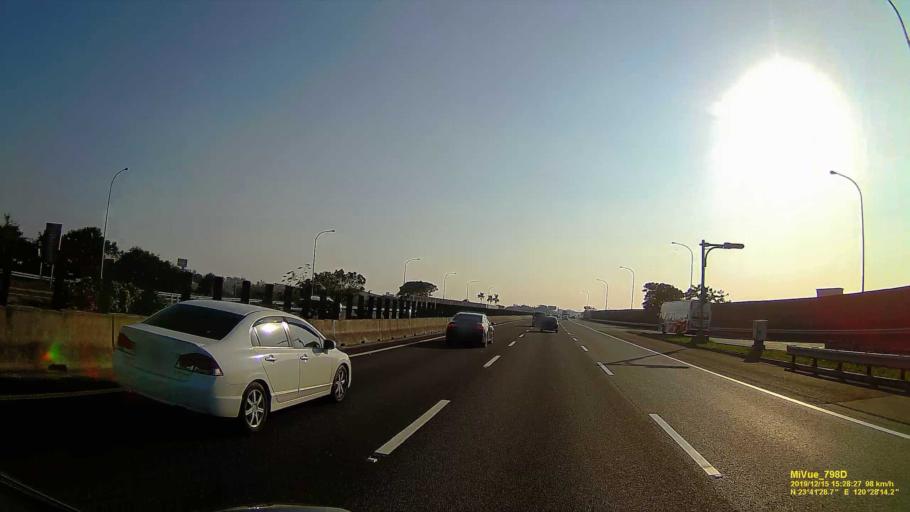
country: TW
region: Taiwan
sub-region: Yunlin
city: Douliu
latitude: 23.6891
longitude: 120.4711
